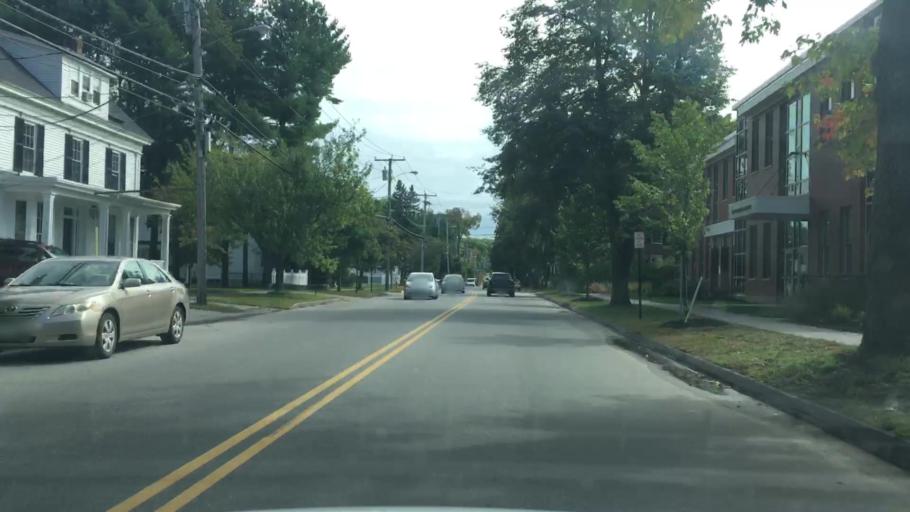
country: US
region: Maine
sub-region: Cumberland County
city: Brunswick
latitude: 43.9167
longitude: -69.9638
